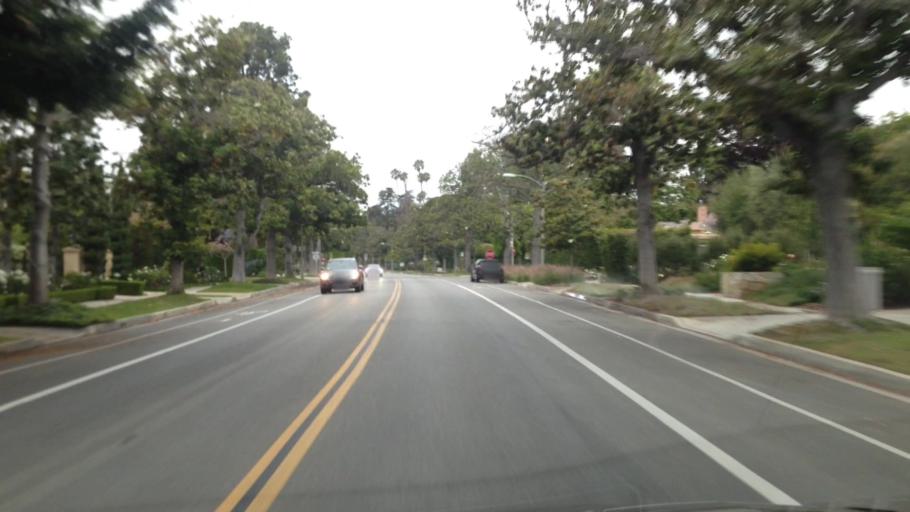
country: US
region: California
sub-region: Los Angeles County
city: Beverly Hills
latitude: 34.0804
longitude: -118.4085
